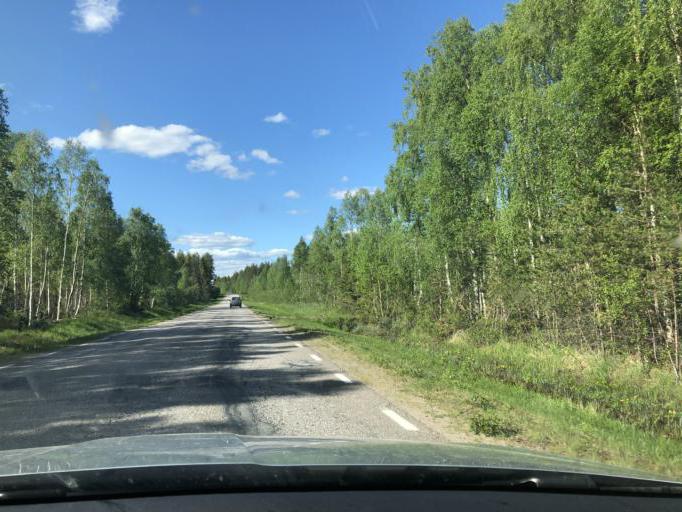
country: SE
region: Norrbotten
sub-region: Kalix Kommun
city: Kalix
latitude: 65.9652
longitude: 23.1474
